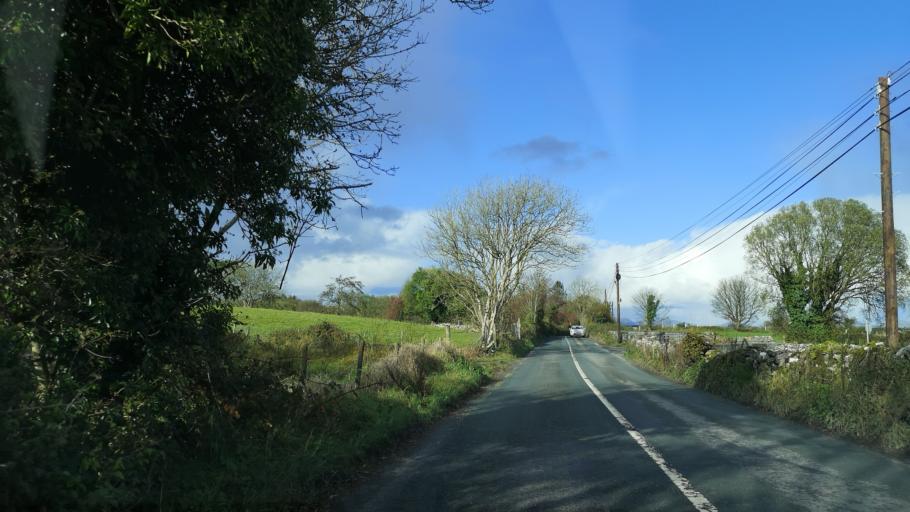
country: IE
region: Connaught
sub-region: Maigh Eo
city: Castlebar
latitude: 53.7700
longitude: -9.3864
